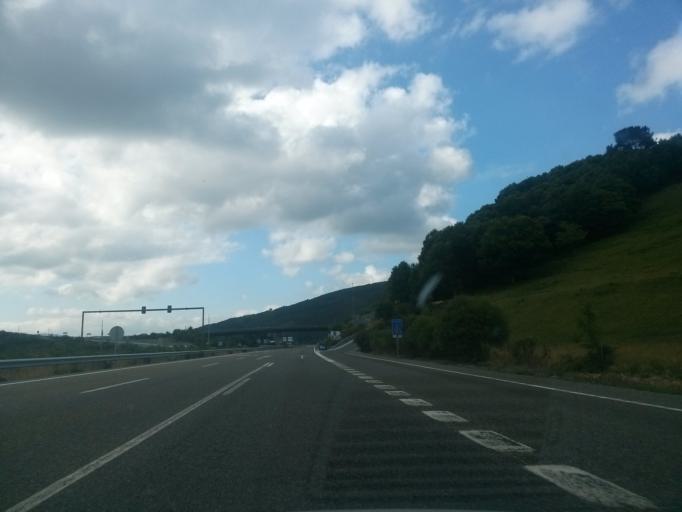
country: ES
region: Galicia
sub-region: Provincia de Lugo
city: Becerrea
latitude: 42.8769
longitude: -7.1760
